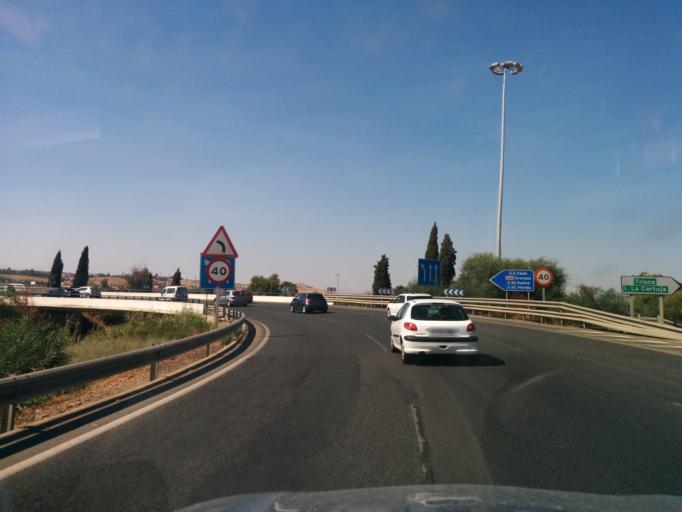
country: ES
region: Andalusia
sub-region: Provincia de Sevilla
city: San Juan de Aznalfarache
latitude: 37.3745
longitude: -6.0144
